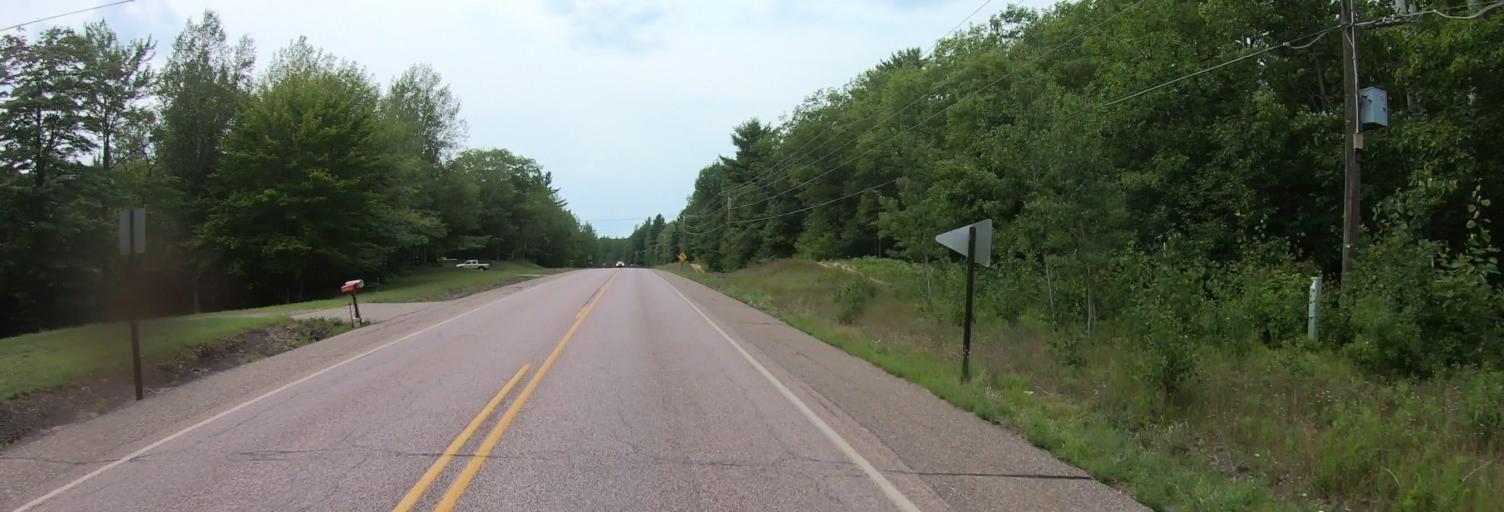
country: US
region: Michigan
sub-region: Marquette County
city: Harvey
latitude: 46.4629
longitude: -87.3798
